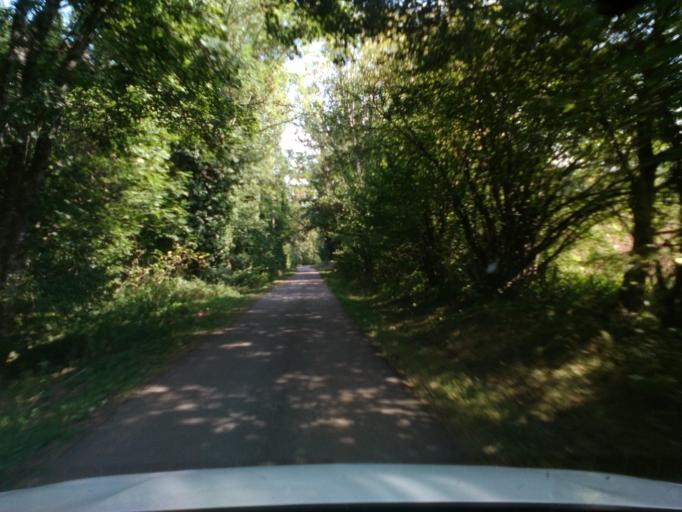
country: FR
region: Lorraine
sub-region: Departement des Vosges
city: Senones
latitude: 48.3546
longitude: 7.0024
